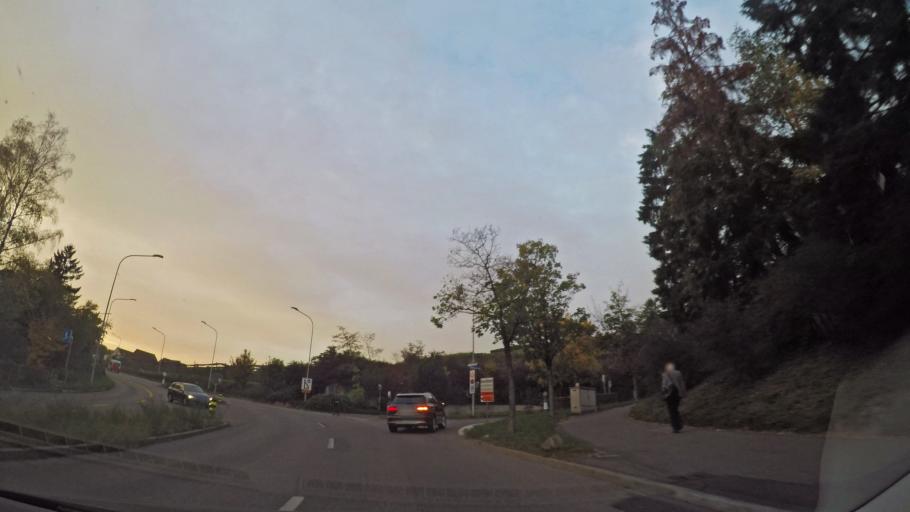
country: CH
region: Zurich
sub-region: Bezirk Zuerich
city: Zuerich (Kreis 10) / Ruetihof
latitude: 47.4066
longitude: 8.4813
